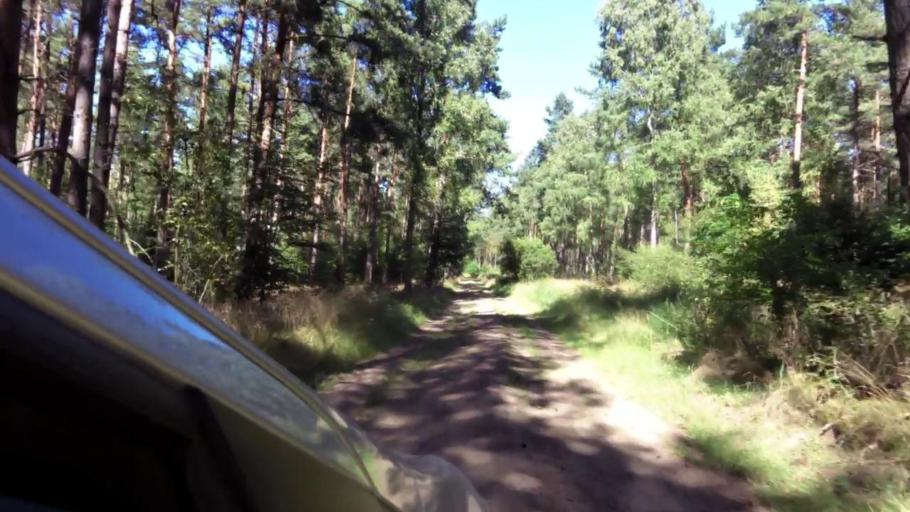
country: PL
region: West Pomeranian Voivodeship
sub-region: Powiat szczecinecki
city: Bialy Bor
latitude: 53.8210
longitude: 16.8642
